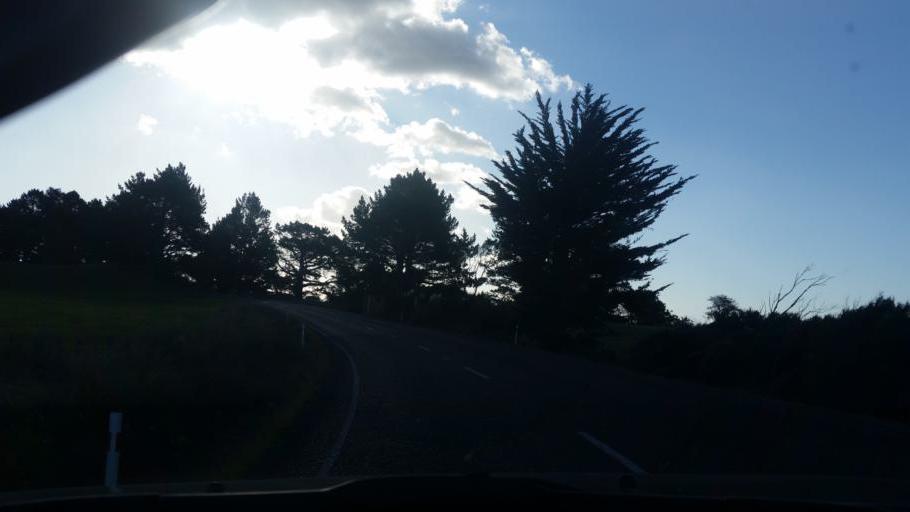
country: NZ
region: Northland
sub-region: Kaipara District
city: Dargaville
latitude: -36.1964
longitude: 174.0512
